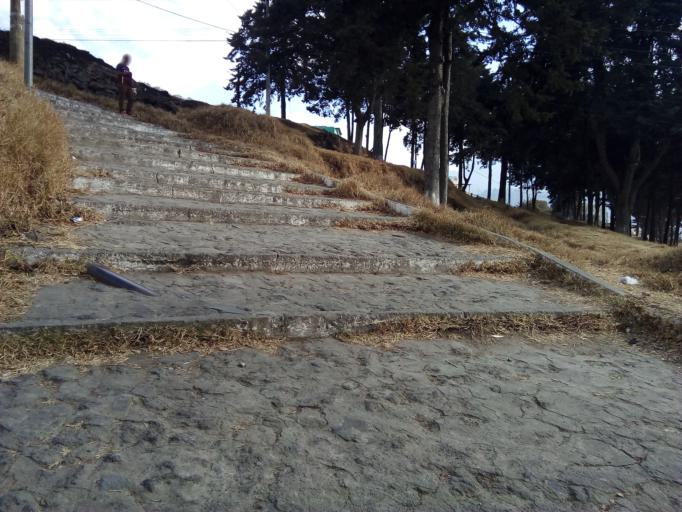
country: GT
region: Quetzaltenango
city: Quetzaltenango
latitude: 14.8372
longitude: -91.5053
